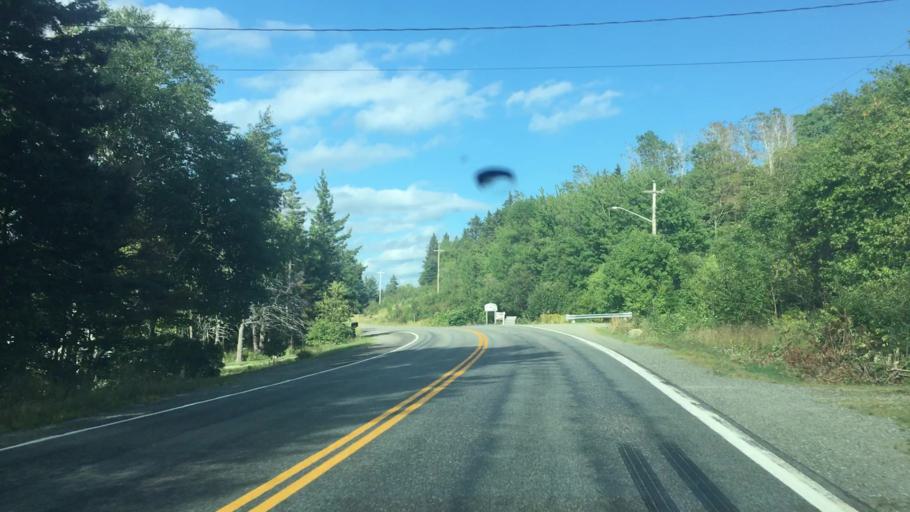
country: CA
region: Nova Scotia
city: Sydney
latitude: 45.8746
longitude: -60.6036
